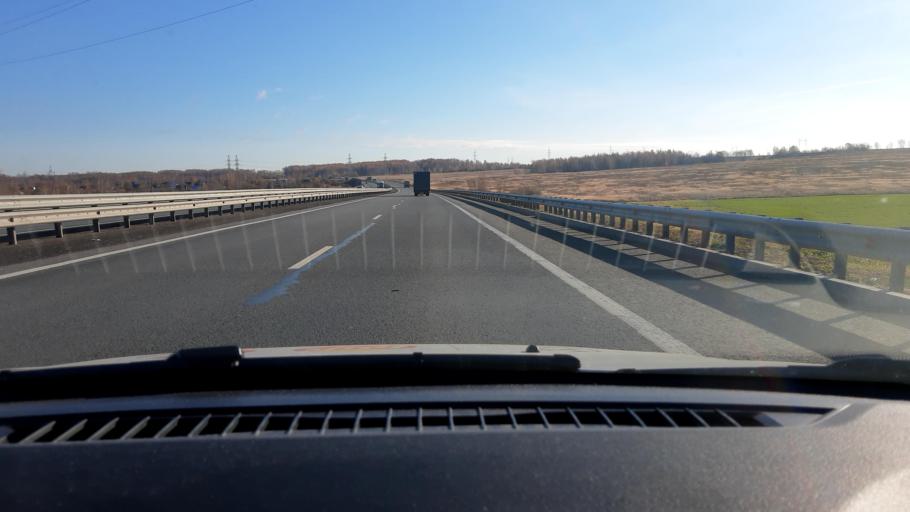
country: RU
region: Nizjnij Novgorod
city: Burevestnik
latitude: 56.1147
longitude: 43.8601
